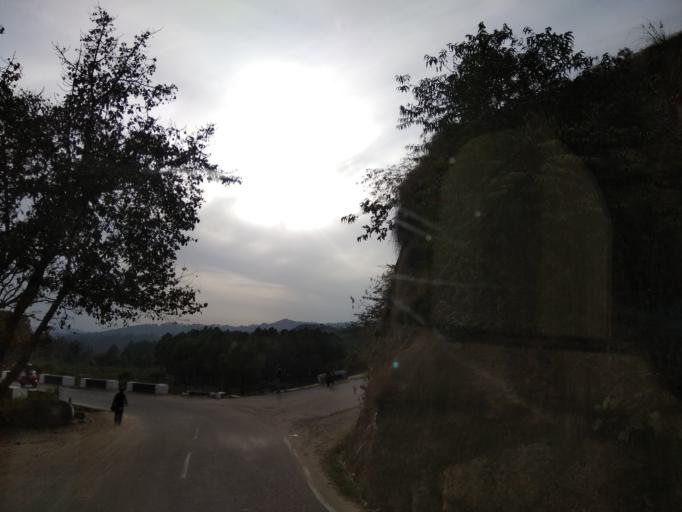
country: IN
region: Himachal Pradesh
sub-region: Kangra
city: Palampur
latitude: 32.1110
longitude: 76.4875
